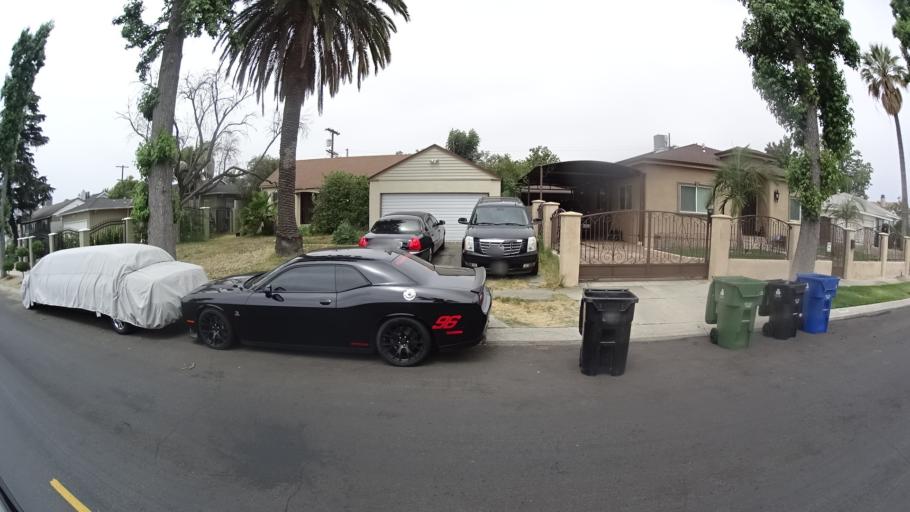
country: US
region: California
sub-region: Los Angeles County
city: North Hollywood
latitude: 34.1914
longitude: -118.4091
